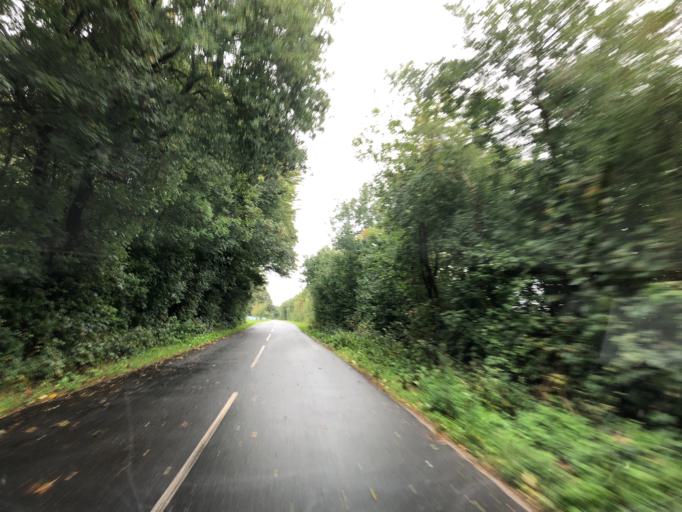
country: DK
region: Central Jutland
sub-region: Herning Kommune
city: Vildbjerg
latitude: 56.1885
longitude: 8.8244
